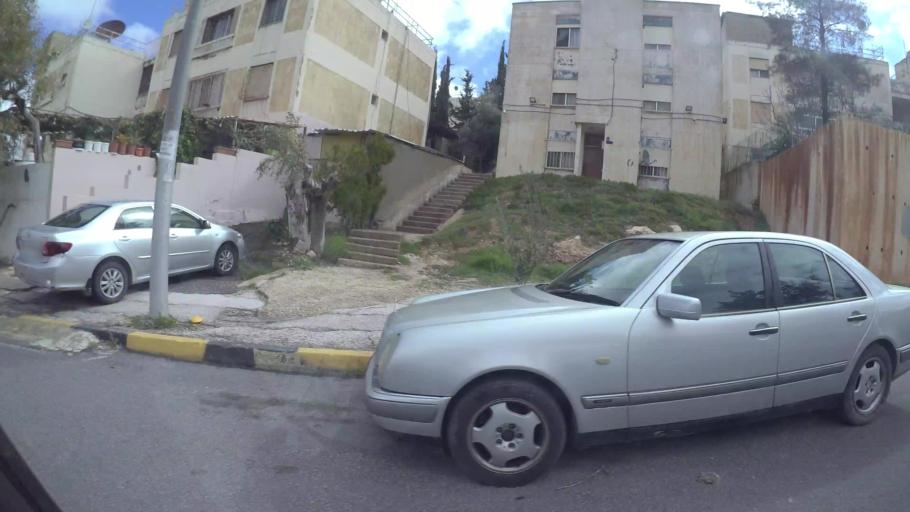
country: JO
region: Amman
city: Al Jubayhah
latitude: 32.0608
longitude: 35.8845
